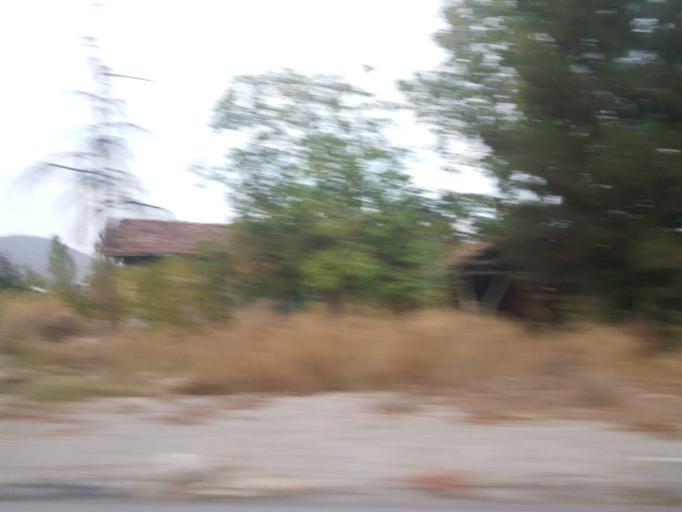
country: TR
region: Amasya
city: Gumushacikoy
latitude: 40.8770
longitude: 35.2323
